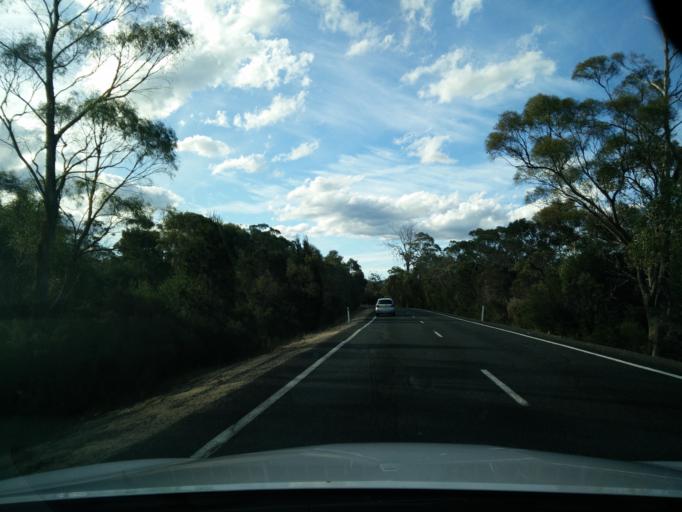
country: AU
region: Tasmania
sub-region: Break O'Day
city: St Helens
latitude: -41.9854
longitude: 148.2419
